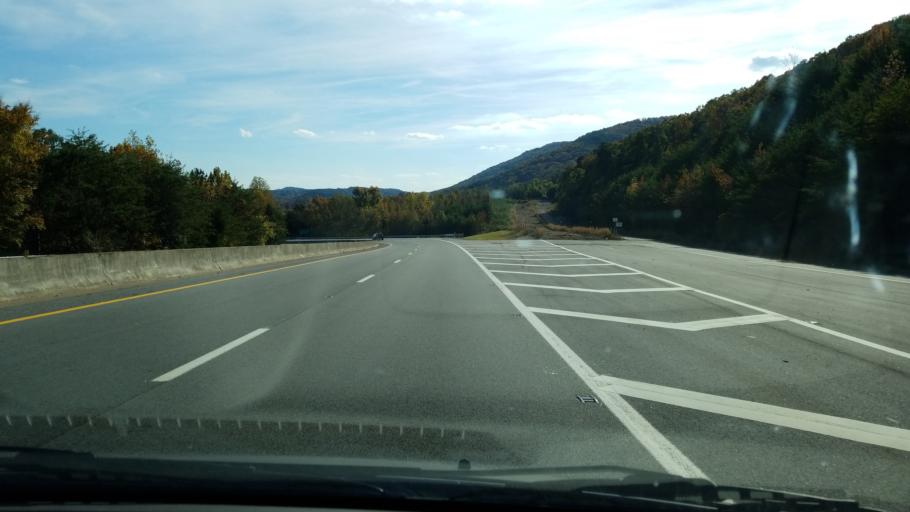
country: US
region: Tennessee
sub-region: Hamilton County
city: Soddy-Daisy
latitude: 35.3085
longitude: -85.1641
